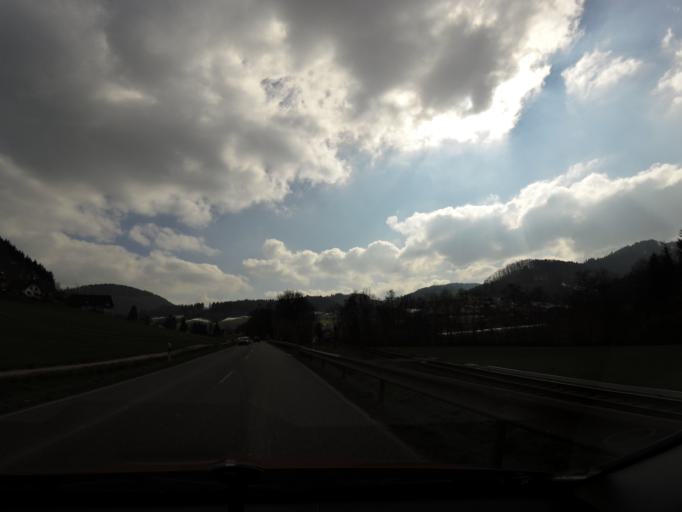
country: DE
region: Baden-Wuerttemberg
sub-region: Freiburg Region
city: Ottenhofen im Schwarzwald
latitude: 48.5710
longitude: 8.1404
